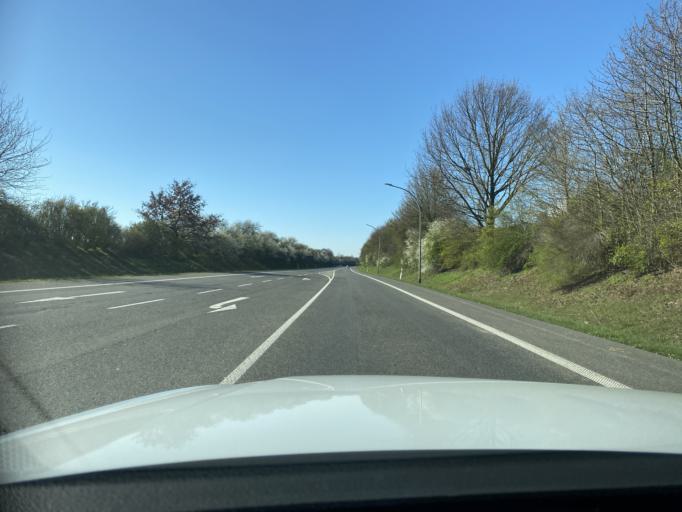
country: DE
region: North Rhine-Westphalia
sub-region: Regierungsbezirk Dusseldorf
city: Neubrueck
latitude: 51.1114
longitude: 6.6357
